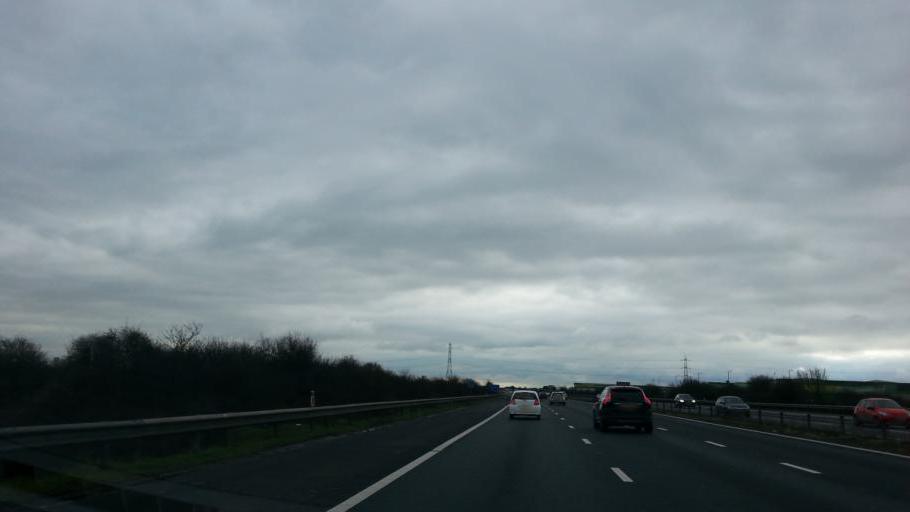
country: GB
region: England
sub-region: Somerset
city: Puriton
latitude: 51.1601
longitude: -2.9816
